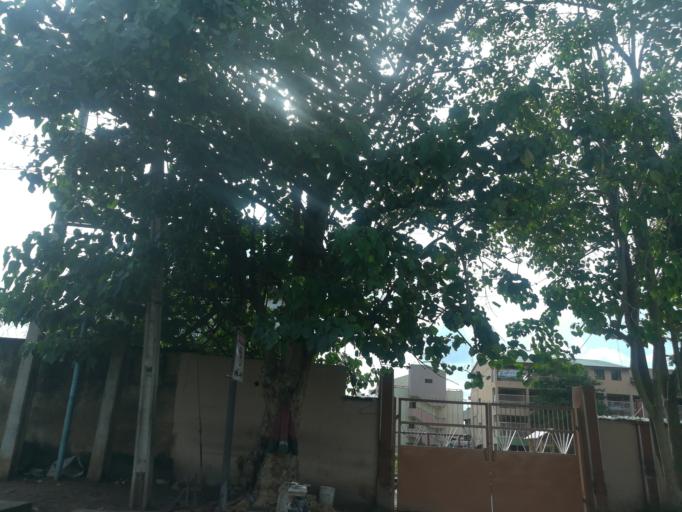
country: NG
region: Lagos
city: Ikeja
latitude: 6.6216
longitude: 3.3579
